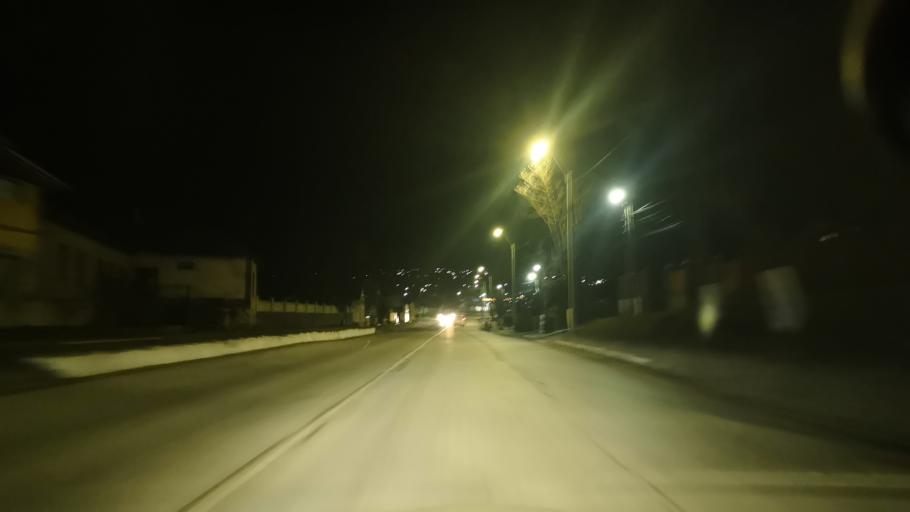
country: MD
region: Orhei
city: Orhei
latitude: 47.3586
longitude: 28.8125
